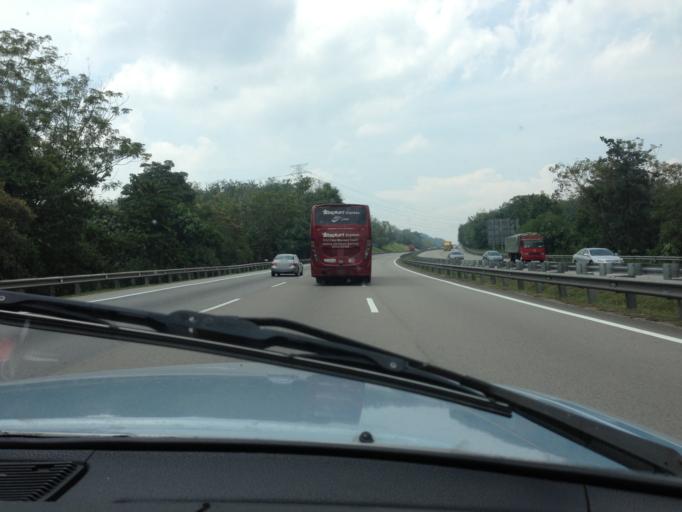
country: MY
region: Melaka
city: Pulau Sebang
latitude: 2.4468
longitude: 102.1740
